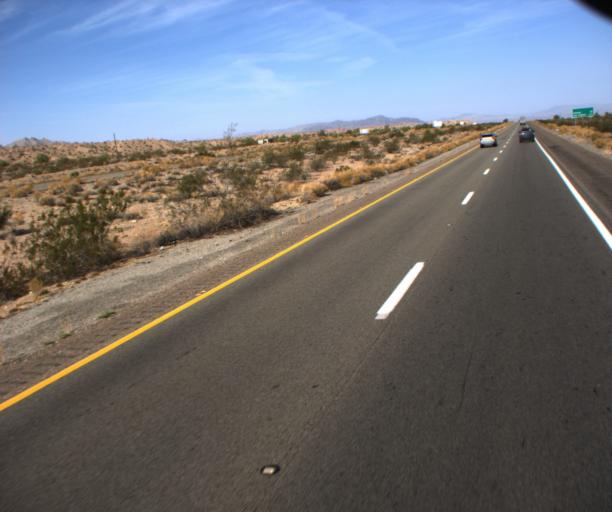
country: US
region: Arizona
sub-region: Mohave County
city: Desert Hills
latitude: 34.7294
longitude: -114.3310
